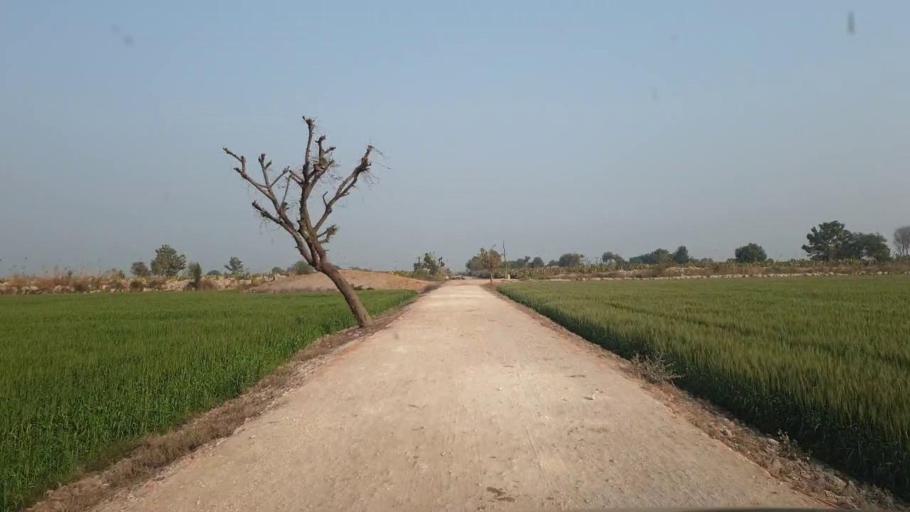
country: PK
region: Sindh
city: Hala
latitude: 25.8951
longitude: 68.4448
